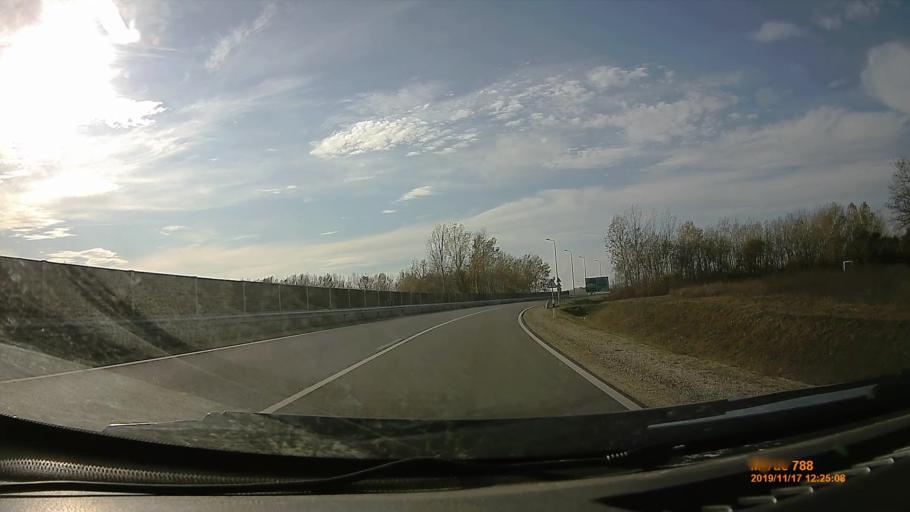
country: HU
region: Bacs-Kiskun
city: Kecskemet
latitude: 46.9314
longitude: 19.6352
